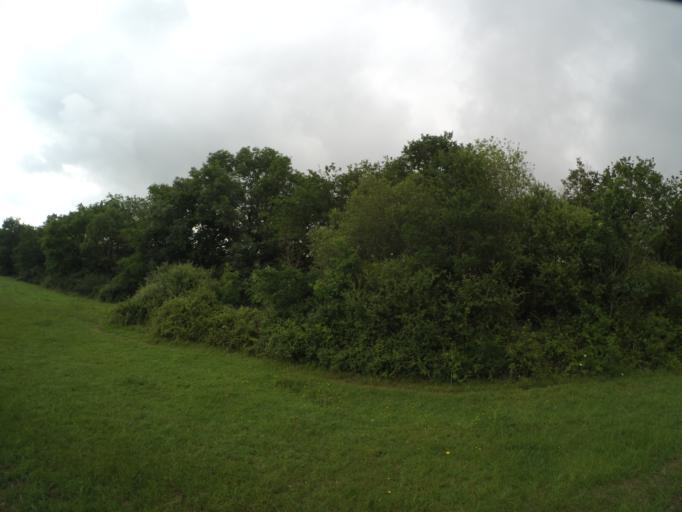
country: FR
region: Pays de la Loire
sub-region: Departement de la Vendee
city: Nesmy
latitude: 46.6026
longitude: -1.3737
